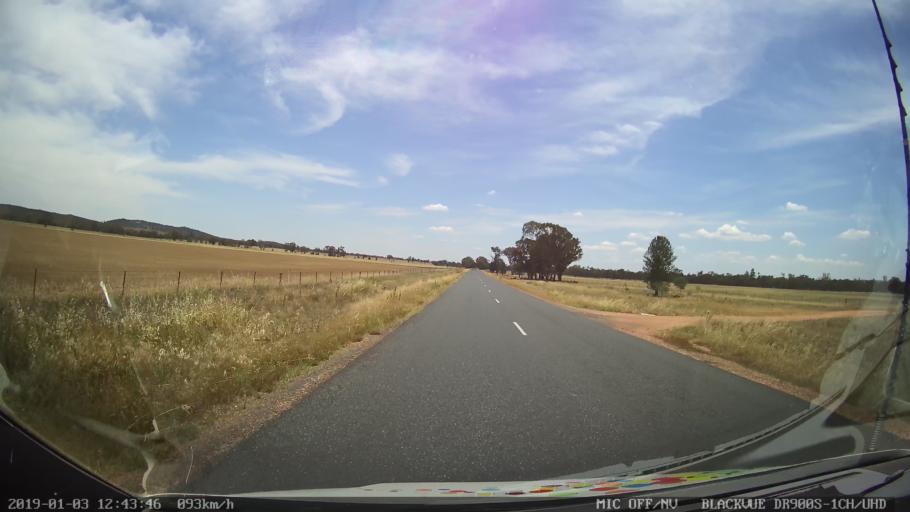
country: AU
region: New South Wales
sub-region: Weddin
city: Grenfell
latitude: -33.7708
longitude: 148.2143
